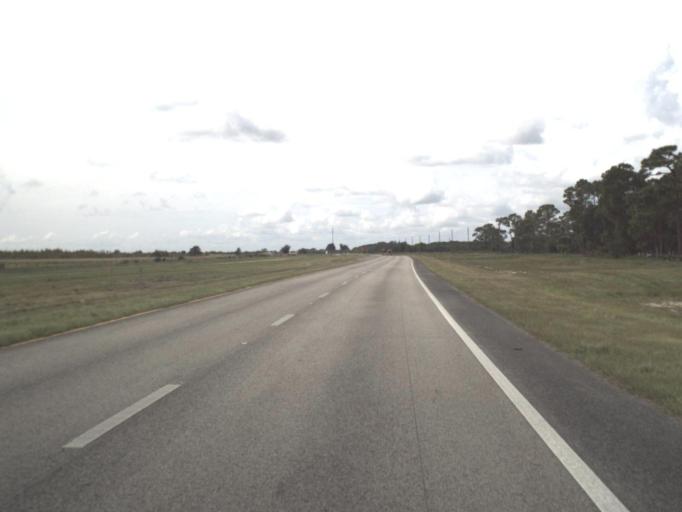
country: US
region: Florida
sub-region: Okeechobee County
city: Taylor Creek
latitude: 27.3008
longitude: -80.6803
